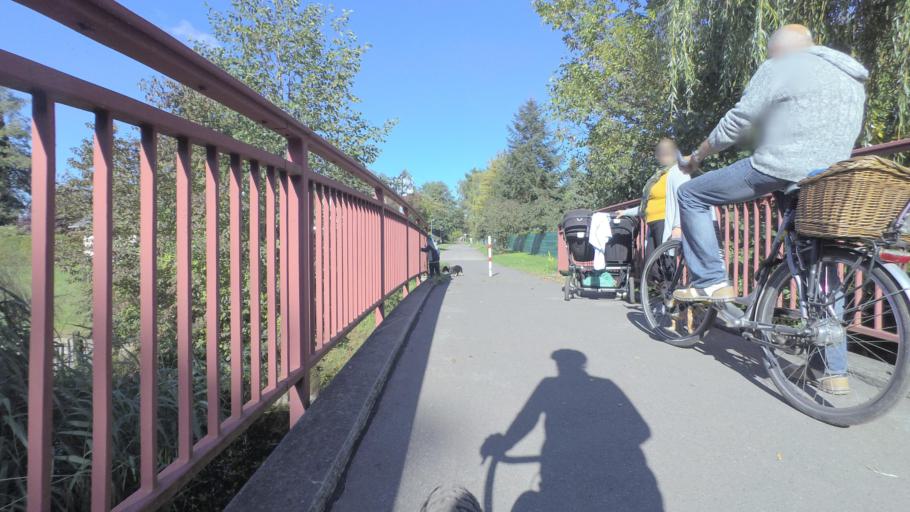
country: DE
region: Brandenburg
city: Rangsdorf
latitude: 52.2853
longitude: 13.4157
